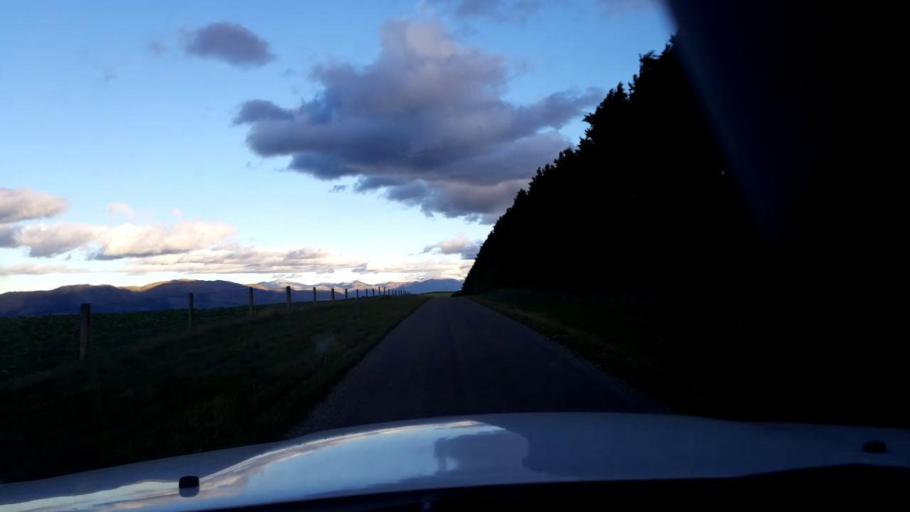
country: NZ
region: Canterbury
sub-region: Timaru District
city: Pleasant Point
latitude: -44.2605
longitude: 170.9167
